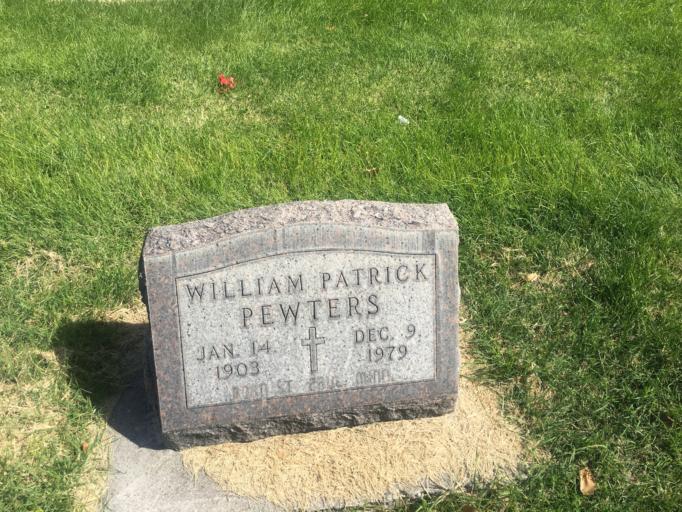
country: US
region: Colorado
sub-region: Mesa County
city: Orchard Mesa
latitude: 39.0438
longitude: -108.5683
